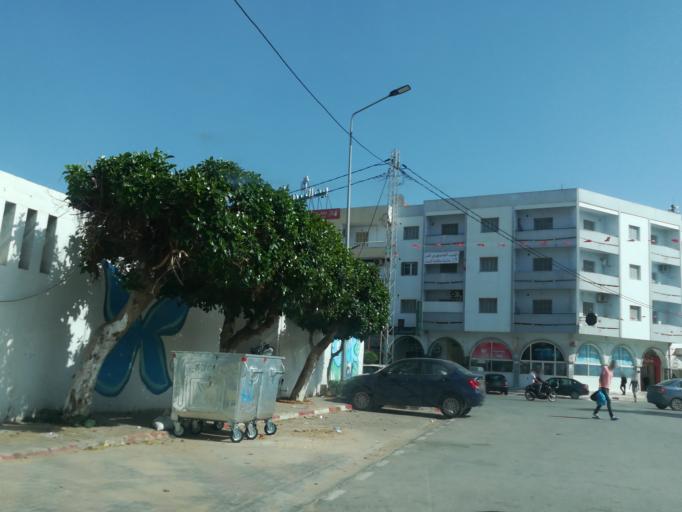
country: TN
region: Safaqis
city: Al Qarmadah
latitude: 34.8039
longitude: 10.7608
